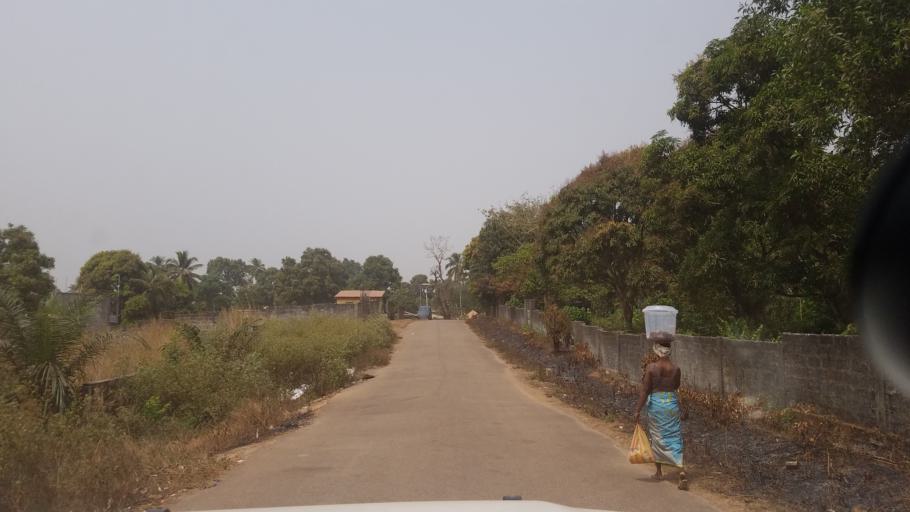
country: GN
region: Kindia
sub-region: Prefecture de Dubreka
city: Dubreka
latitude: 9.7871
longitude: -13.5161
